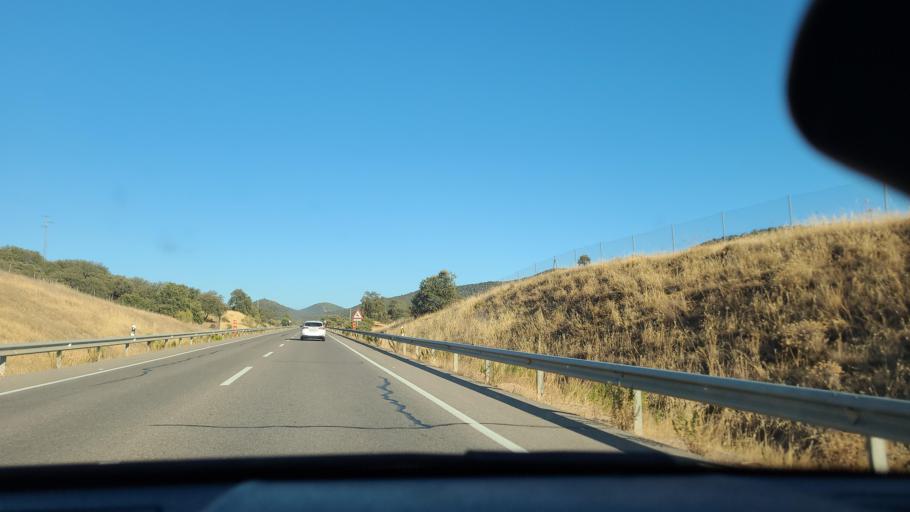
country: ES
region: Andalusia
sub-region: Province of Cordoba
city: Villaharta
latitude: 38.1328
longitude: -4.9400
